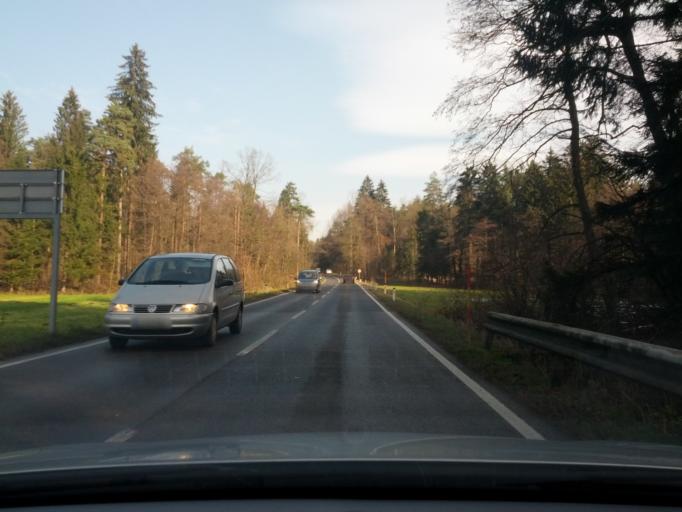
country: SI
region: Ljubljana
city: Ljubljana
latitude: 46.0605
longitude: 14.4672
